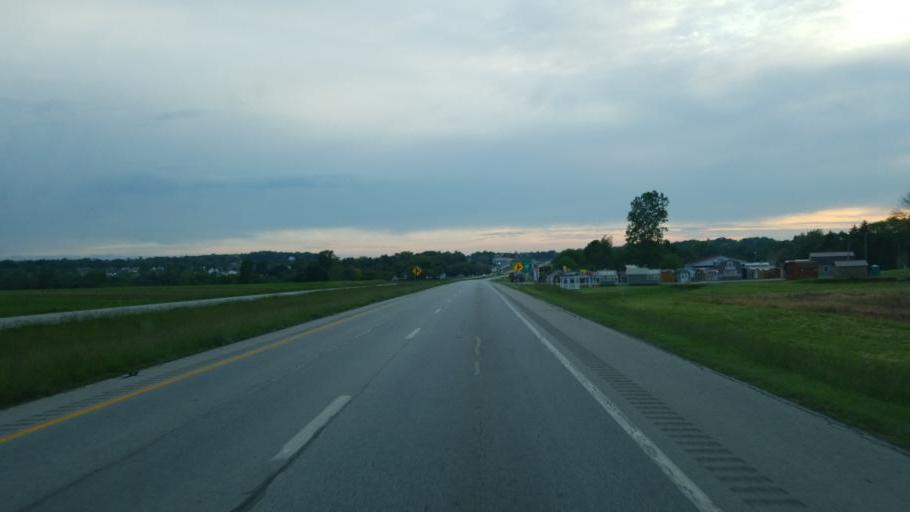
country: US
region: Ohio
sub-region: Wayne County
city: Dalton
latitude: 40.7961
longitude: -81.6827
